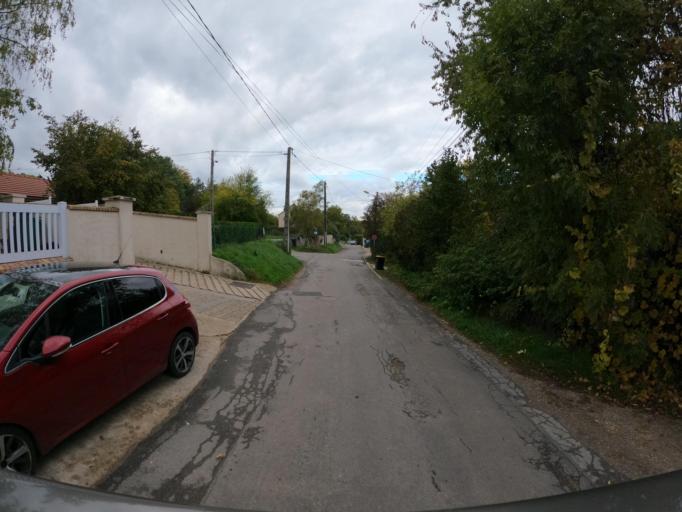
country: FR
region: Ile-de-France
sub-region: Departement de Seine-et-Marne
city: Saint-Germain-sur-Morin
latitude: 48.8736
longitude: 2.8431
